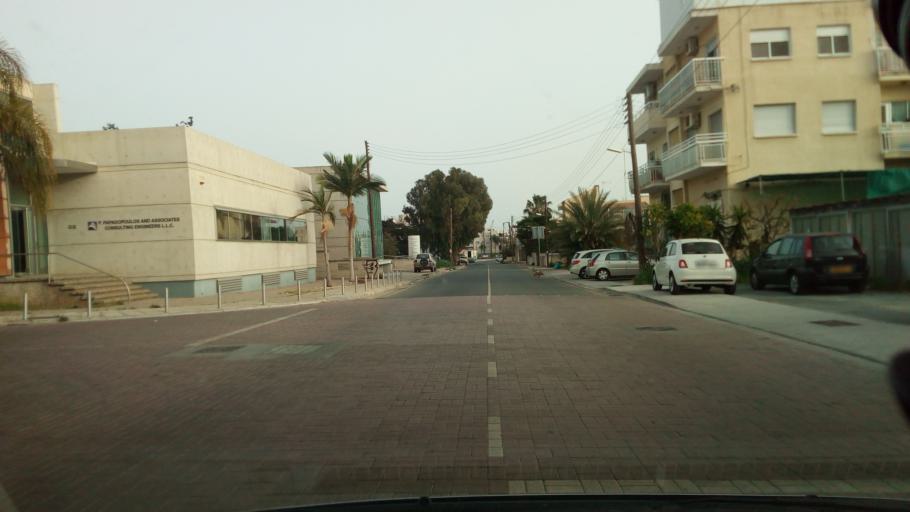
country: CY
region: Limassol
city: Limassol
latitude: 34.6579
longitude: 33.0037
